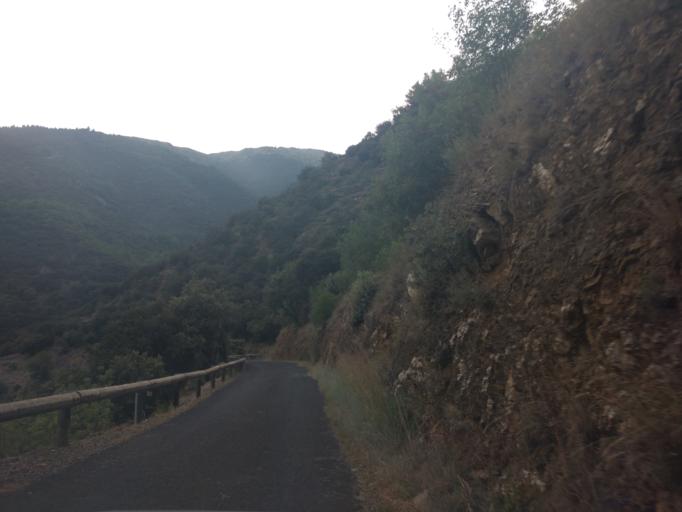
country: FR
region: Languedoc-Roussillon
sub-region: Departement des Pyrenees-Orientales
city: Vernet-les-Bains
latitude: 42.5665
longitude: 2.2941
